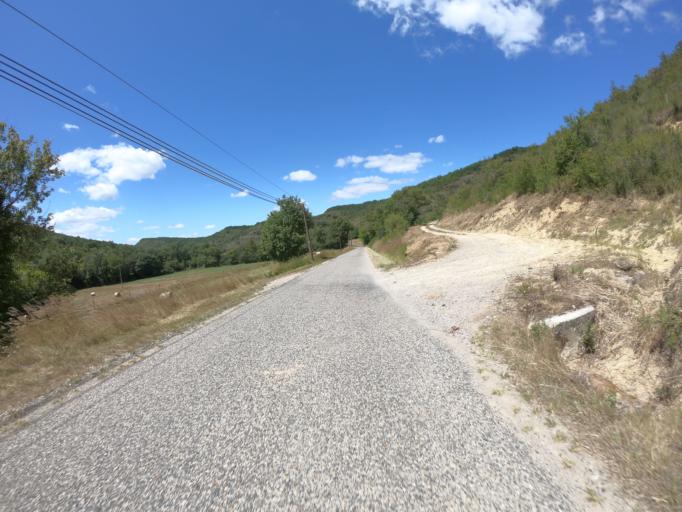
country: FR
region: Midi-Pyrenees
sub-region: Departement de l'Ariege
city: Mirepoix
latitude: 43.0508
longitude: 1.8163
